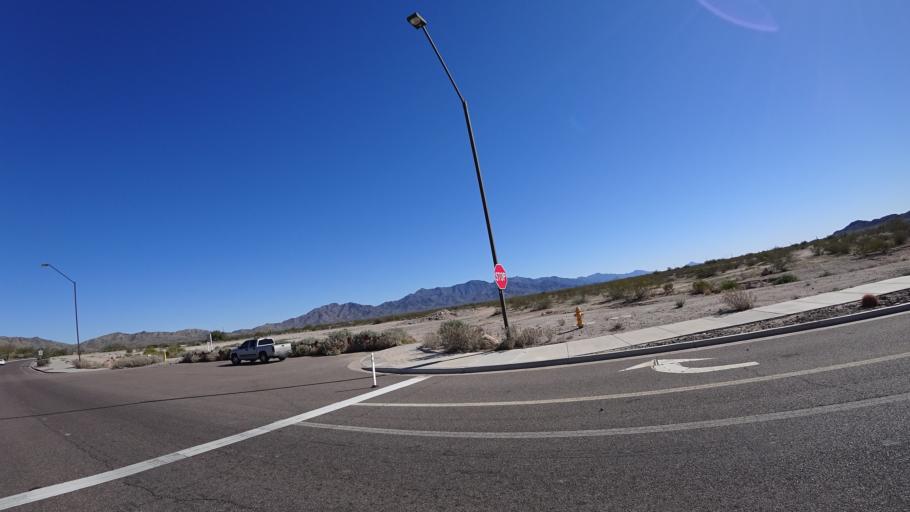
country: US
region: Arizona
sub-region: Maricopa County
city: Goodyear
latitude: 33.3180
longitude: -112.4315
